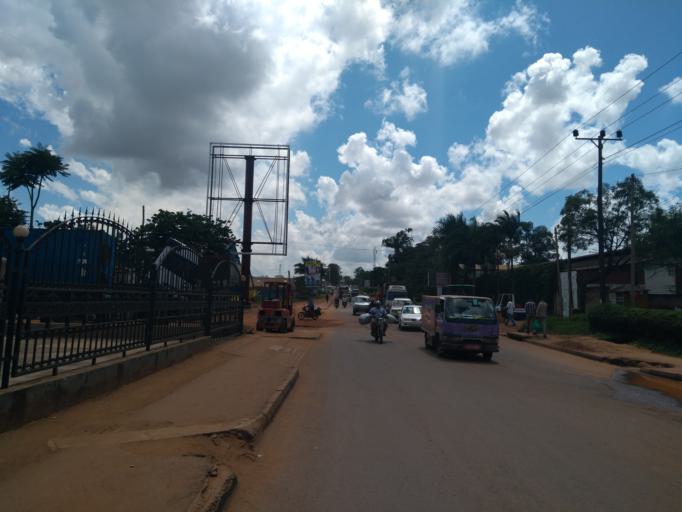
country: UG
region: Central Region
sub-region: Kampala District
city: Kampala
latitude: 0.3150
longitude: 32.6112
